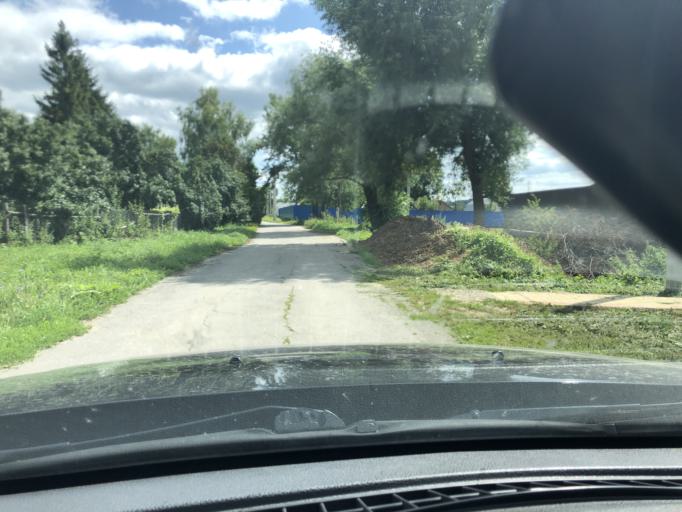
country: RU
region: Tula
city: Revyakino
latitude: 54.3486
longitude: 37.6160
